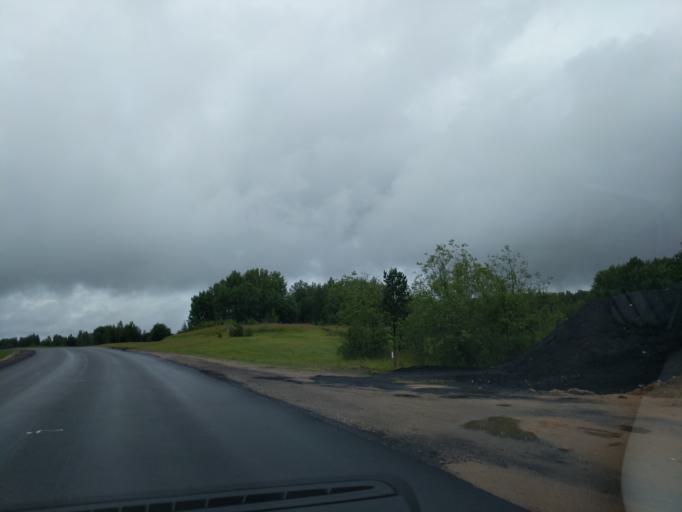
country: BY
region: Minsk
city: Syomkava
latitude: 54.2562
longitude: 27.4941
